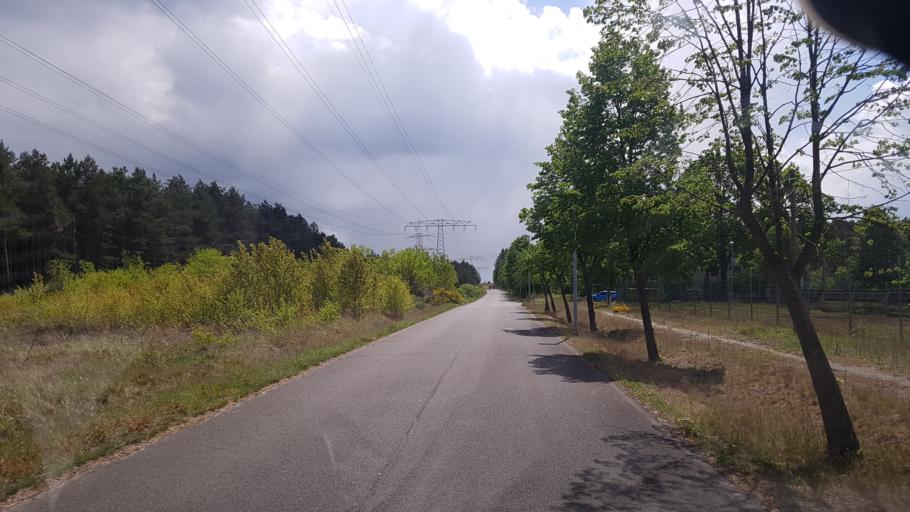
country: DE
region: Brandenburg
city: Altdobern
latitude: 51.6480
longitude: 14.0033
